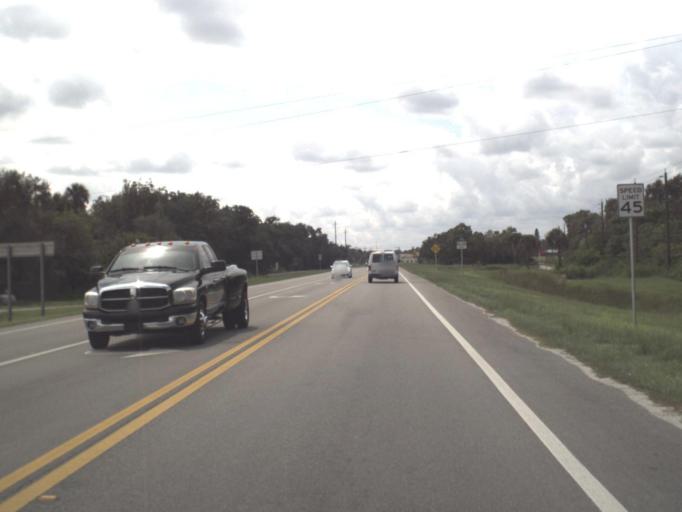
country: US
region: Florida
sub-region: Hendry County
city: LaBelle
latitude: 26.7755
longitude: -81.4375
